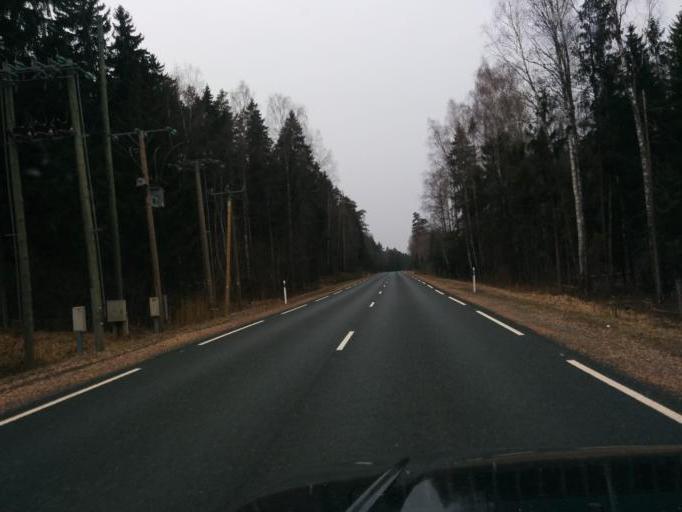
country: LV
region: Ikskile
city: Ikskile
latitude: 56.8006
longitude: 24.5209
